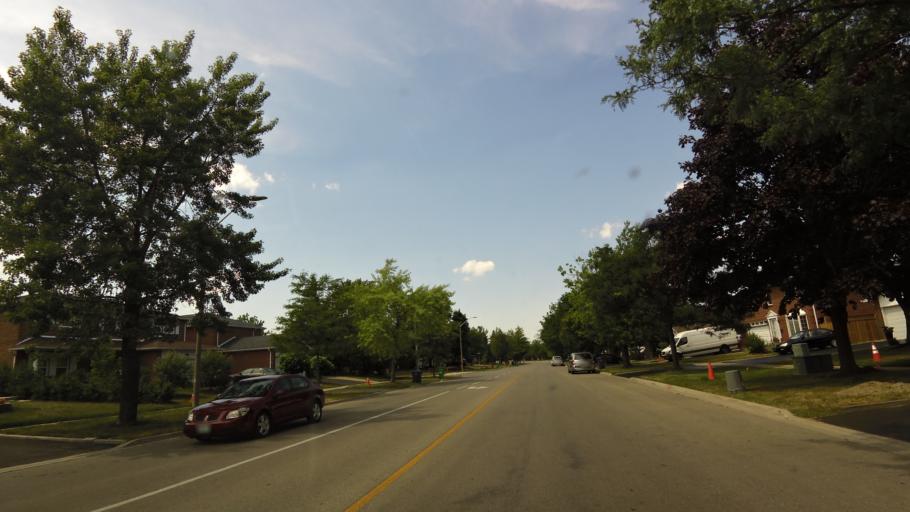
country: CA
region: Ontario
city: Etobicoke
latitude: 43.6302
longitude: -79.5978
